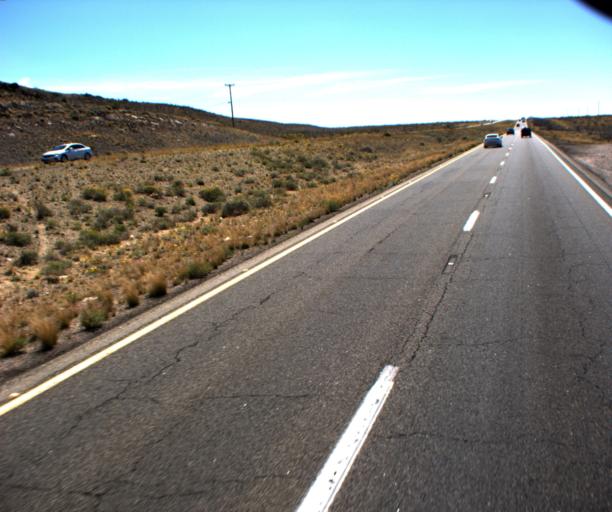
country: US
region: Arizona
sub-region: Mohave County
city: Dolan Springs
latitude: 35.4342
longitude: -114.2866
